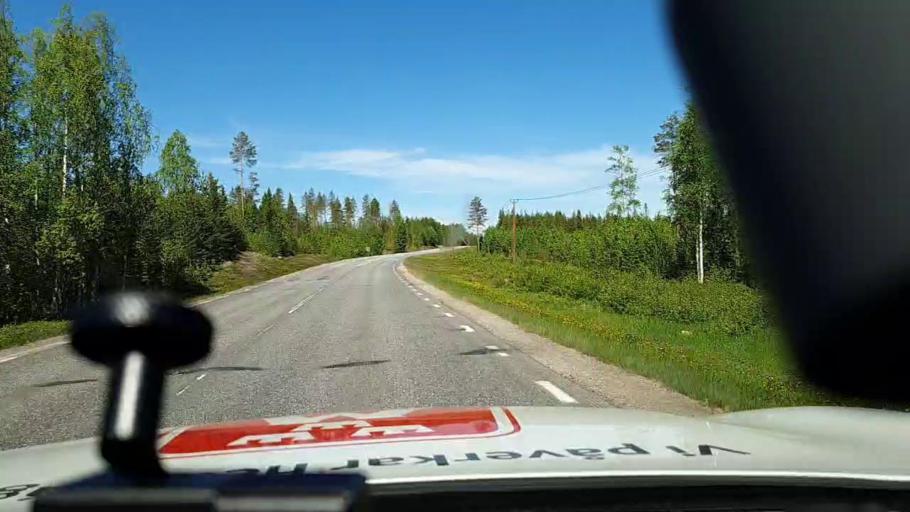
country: SE
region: Norrbotten
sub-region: Kalix Kommun
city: Toere
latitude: 66.0942
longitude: 22.7126
